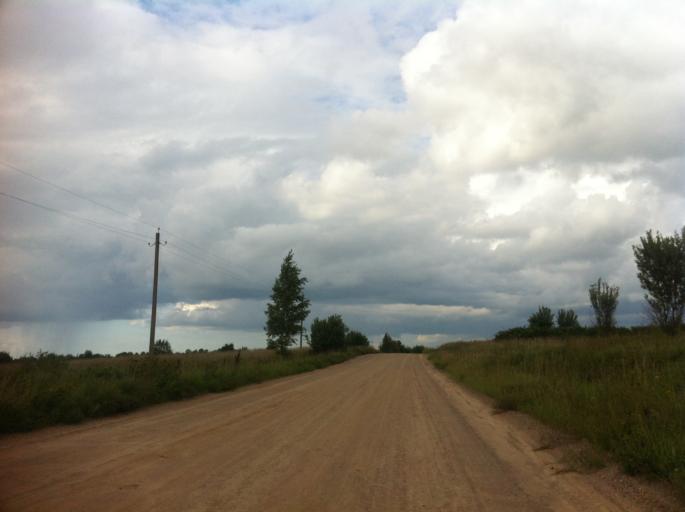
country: RU
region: Pskov
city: Izborsk
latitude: 57.8214
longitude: 27.9784
